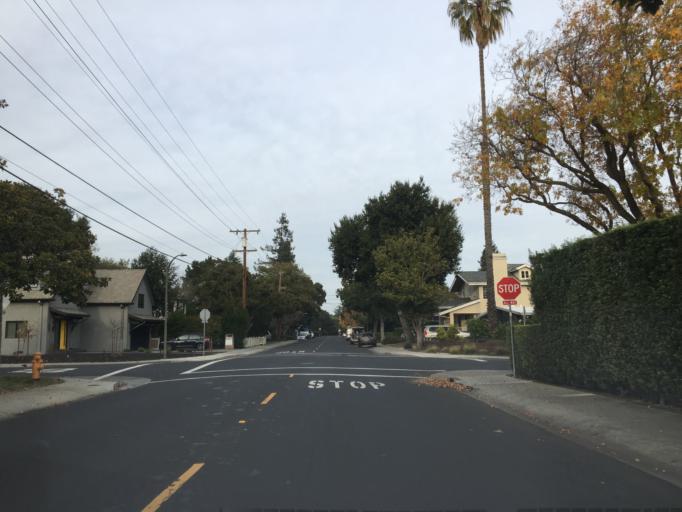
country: US
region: California
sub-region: Santa Clara County
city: Palo Alto
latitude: 37.4450
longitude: -122.1292
